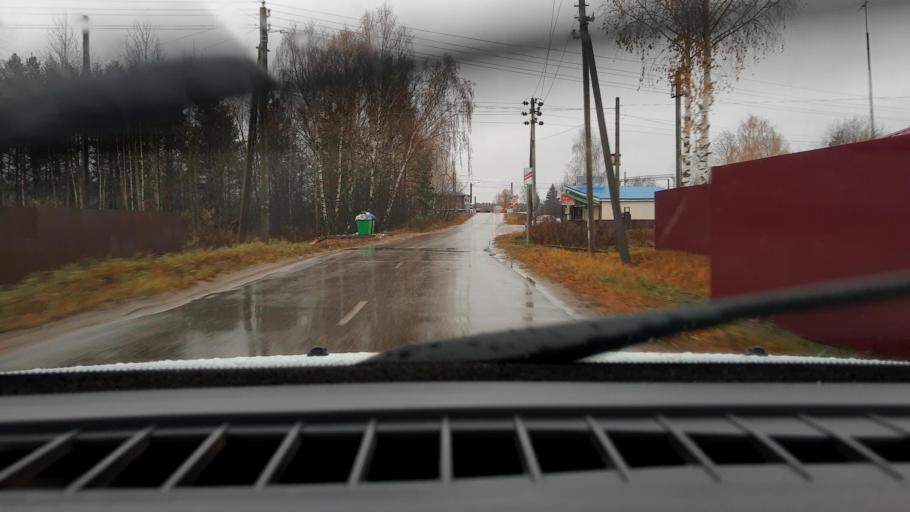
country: RU
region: Nizjnij Novgorod
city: Linda
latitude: 56.6869
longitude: 44.2025
